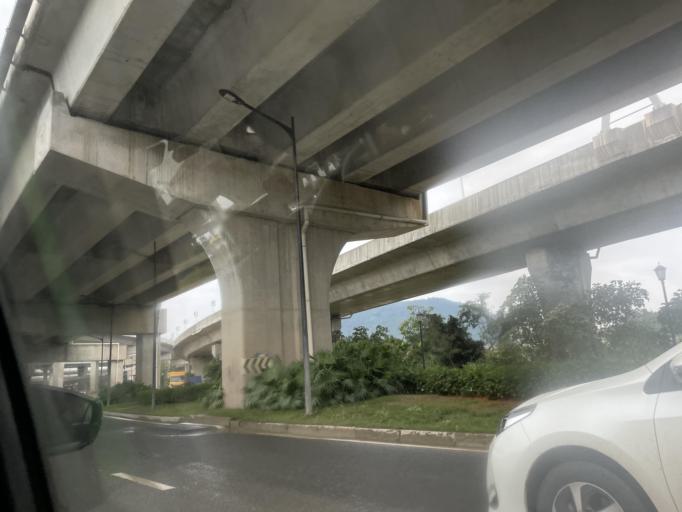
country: CN
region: Guangdong
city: Nanping
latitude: 22.1765
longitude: 113.4662
